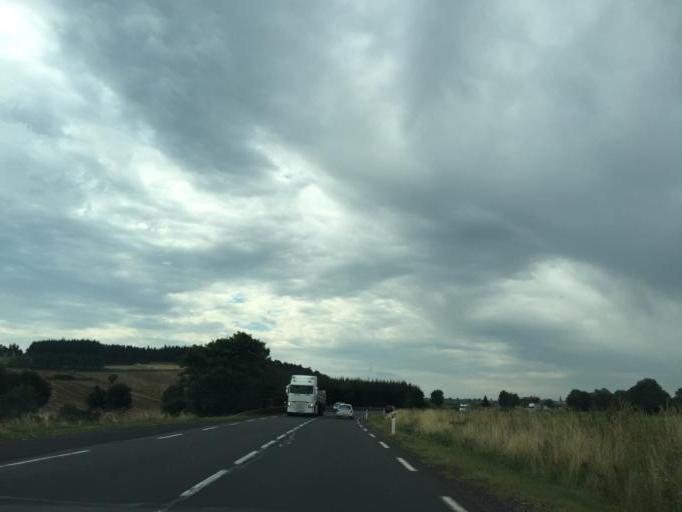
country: FR
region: Auvergne
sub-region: Departement de la Haute-Loire
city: Solignac-sur-Loire
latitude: 44.9033
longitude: 3.8512
